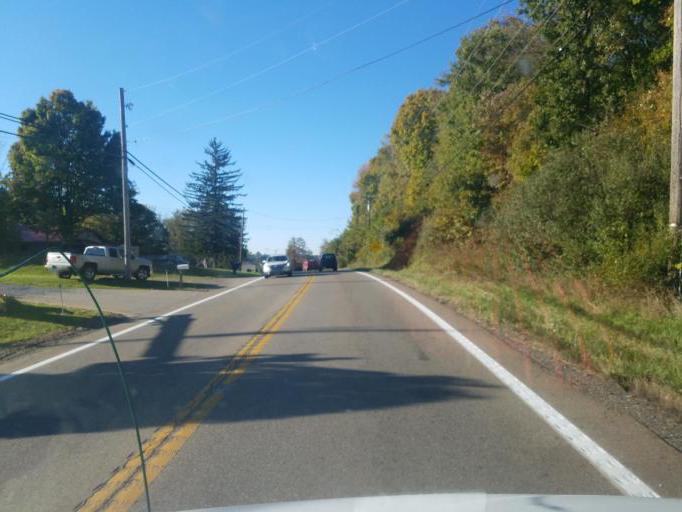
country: US
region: Ohio
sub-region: Columbiana County
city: New Waterford
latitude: 40.8027
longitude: -80.6331
